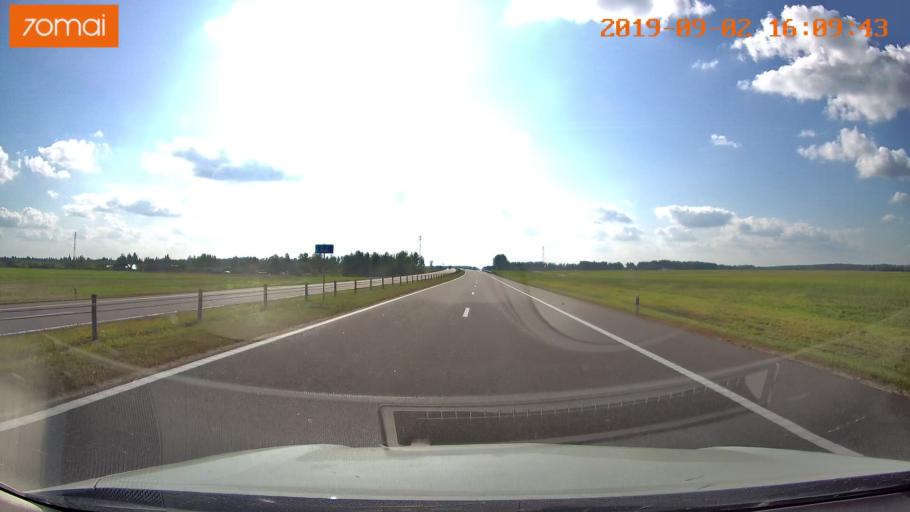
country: BY
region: Minsk
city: Chervyen'
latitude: 53.7683
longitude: 28.6929
